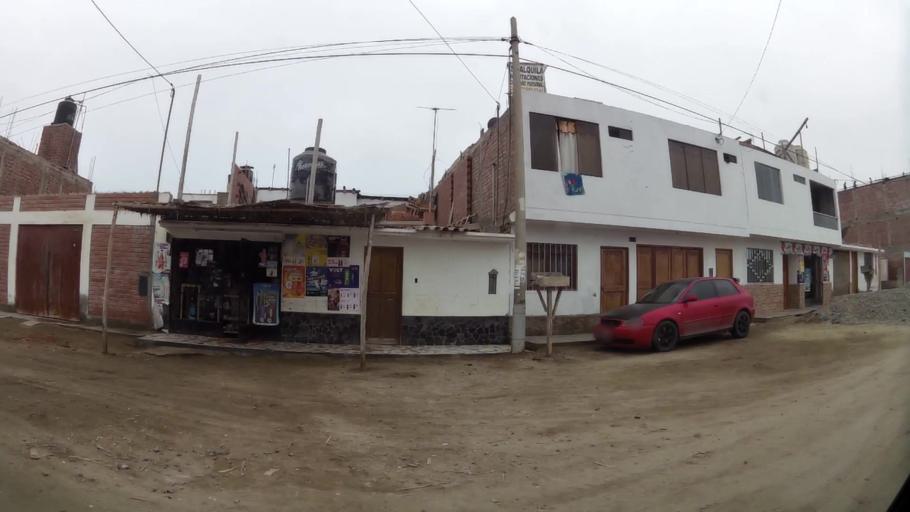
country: PE
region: Lima
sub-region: Lima
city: Punta Hermosa
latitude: -12.3306
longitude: -76.8263
